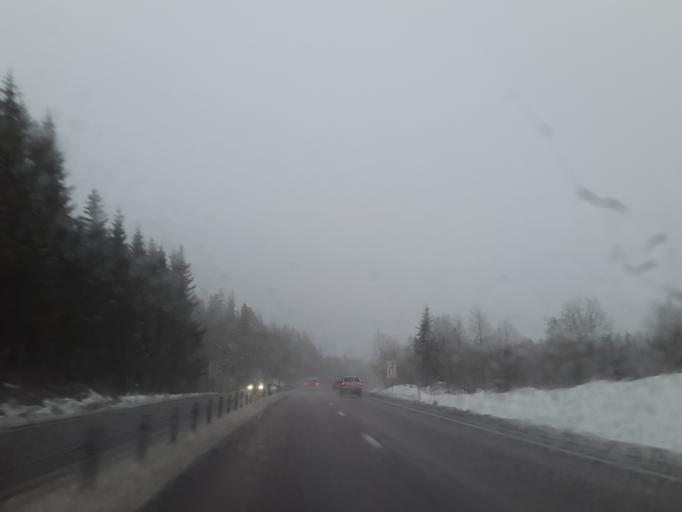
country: SE
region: Joenkoeping
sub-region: Mullsjo Kommun
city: Mullsjoe
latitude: 57.7715
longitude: 13.7121
